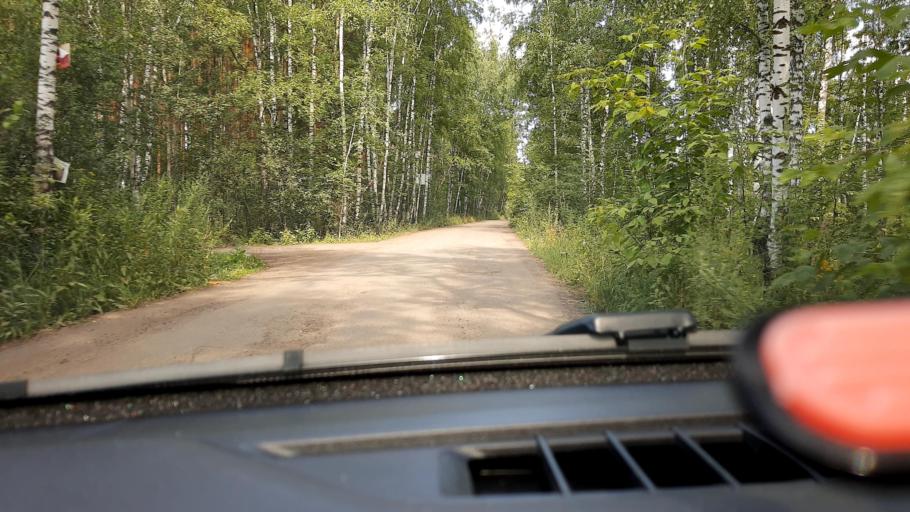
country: RU
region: Nizjnij Novgorod
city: Gorbatovka
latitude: 56.2977
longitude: 43.8198
